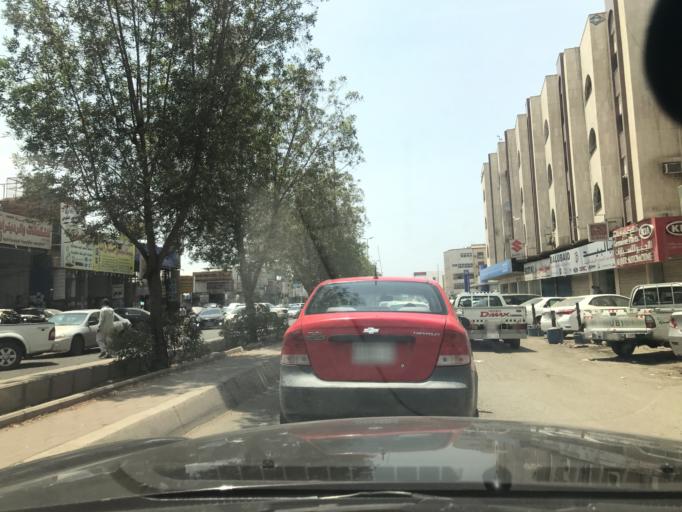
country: SA
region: Makkah
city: Jeddah
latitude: 21.4580
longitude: 39.2230
